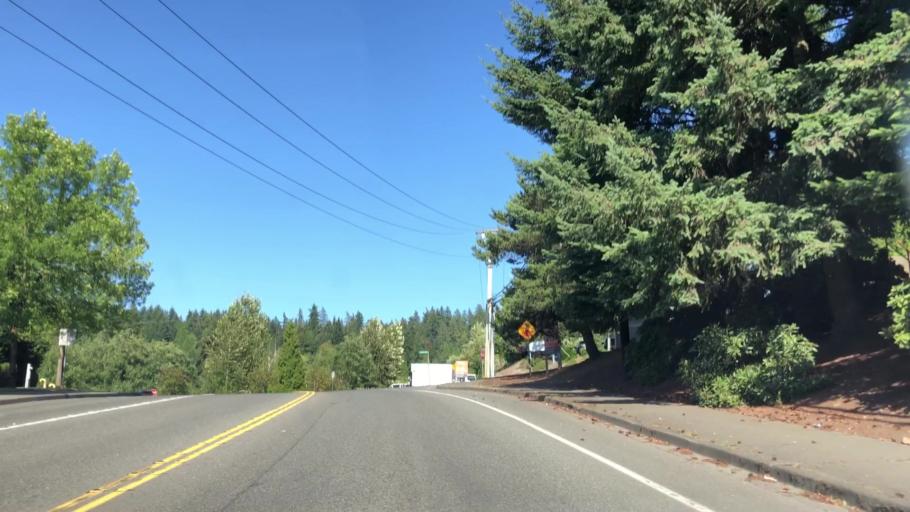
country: US
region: Washington
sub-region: King County
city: Woodinville
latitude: 47.7650
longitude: -122.1513
